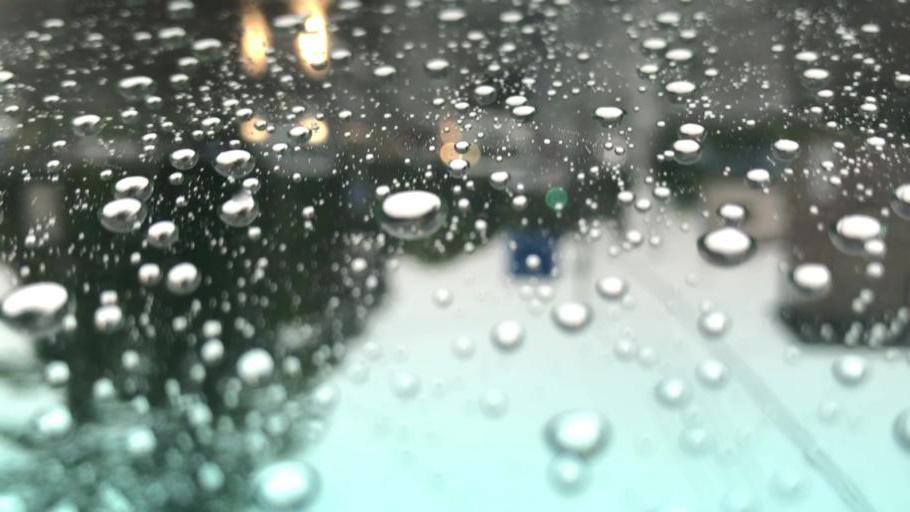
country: JP
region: Hokkaido
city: Nayoro
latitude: 44.2905
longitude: 142.4175
